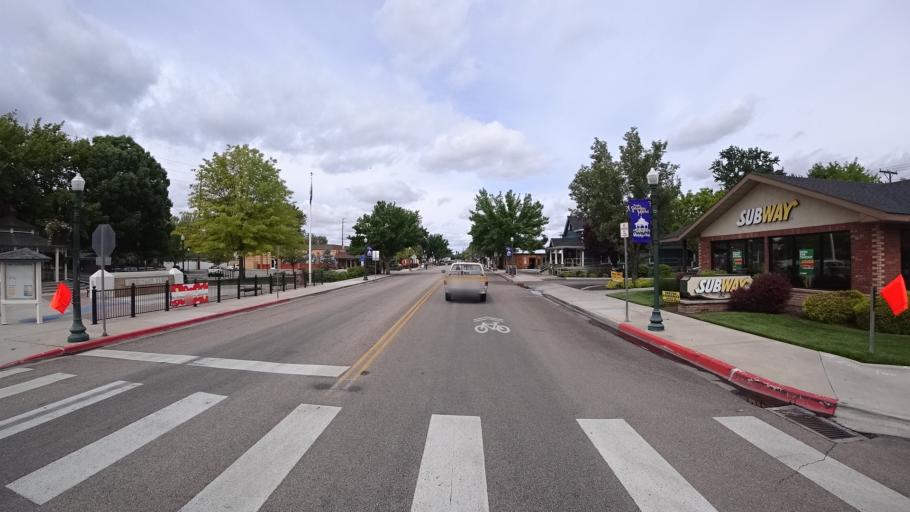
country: US
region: Idaho
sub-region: Ada County
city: Eagle
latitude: 43.6952
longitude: -116.3514
